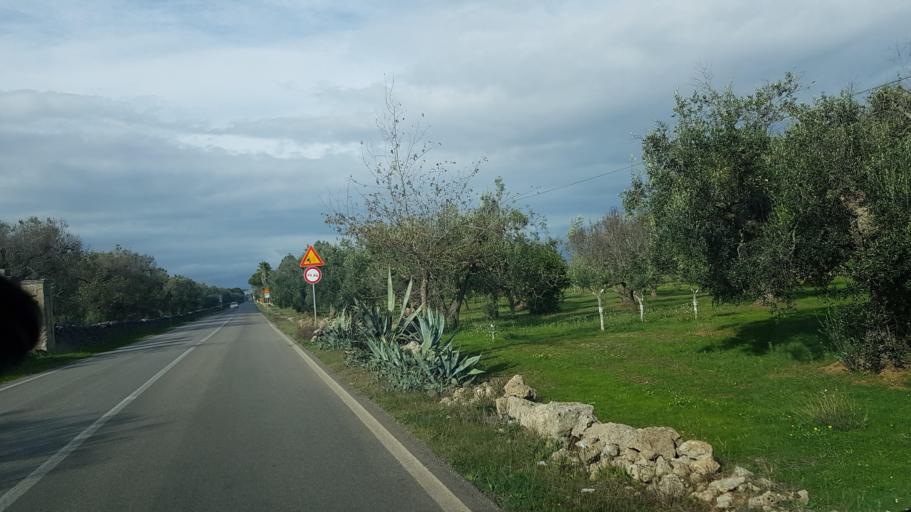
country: IT
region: Apulia
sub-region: Provincia di Brindisi
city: Oria
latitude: 40.4810
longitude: 17.6871
